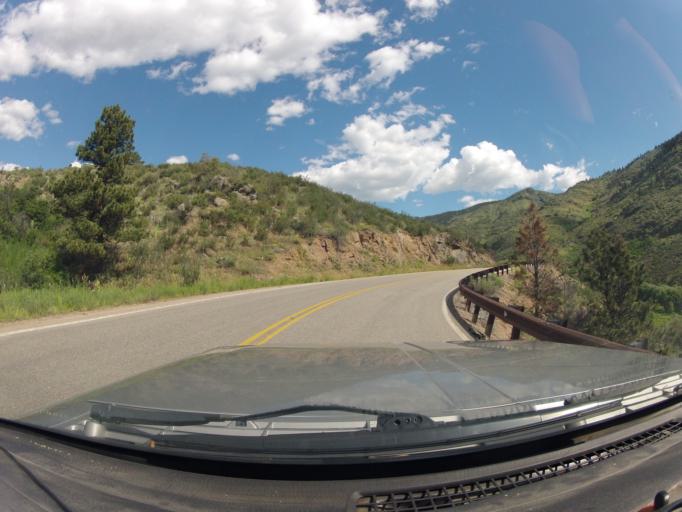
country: US
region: Colorado
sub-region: Larimer County
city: Laporte
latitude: 40.5491
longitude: -105.2883
